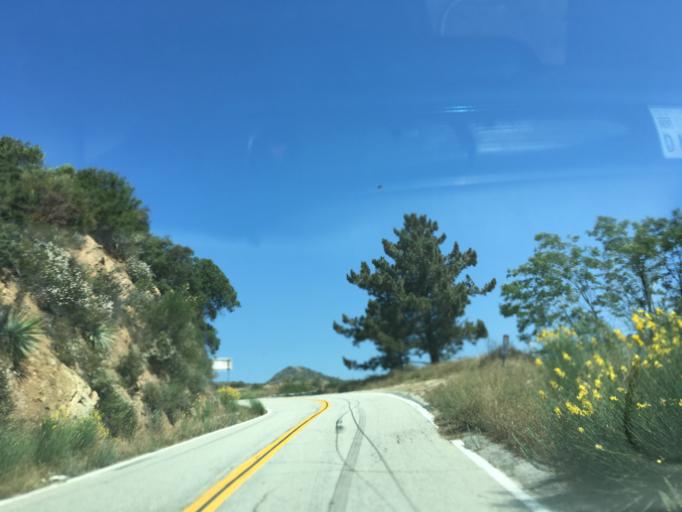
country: US
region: California
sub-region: Los Angeles County
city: Glendora
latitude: 34.2043
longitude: -117.8090
